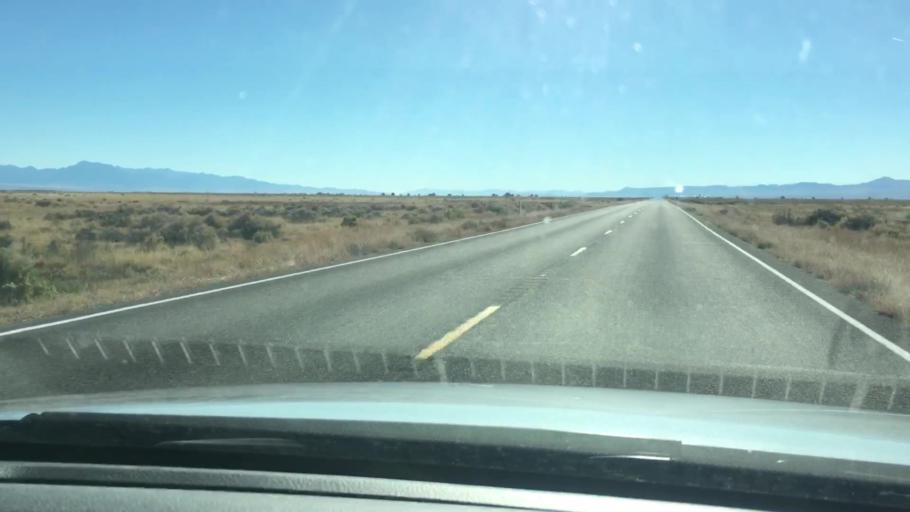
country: US
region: Nevada
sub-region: White Pine County
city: Ely
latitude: 38.6524
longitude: -115.5796
